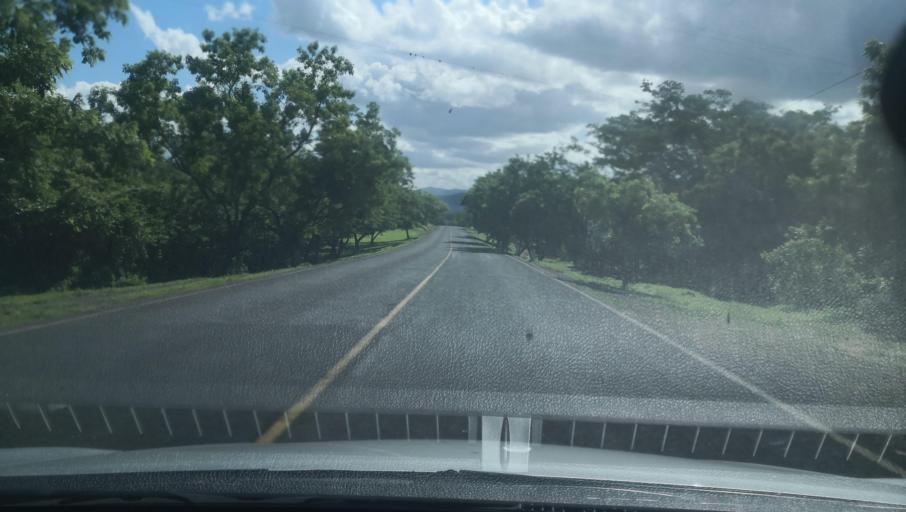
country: NI
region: Madriz
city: Somoto
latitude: 13.4724
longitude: -86.6153
